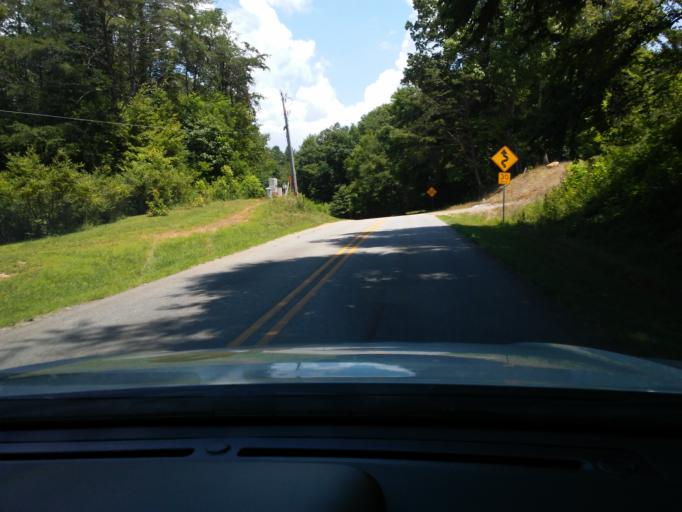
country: US
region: Georgia
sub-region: Towns County
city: Hiawassee
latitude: 34.8675
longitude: -83.7502
